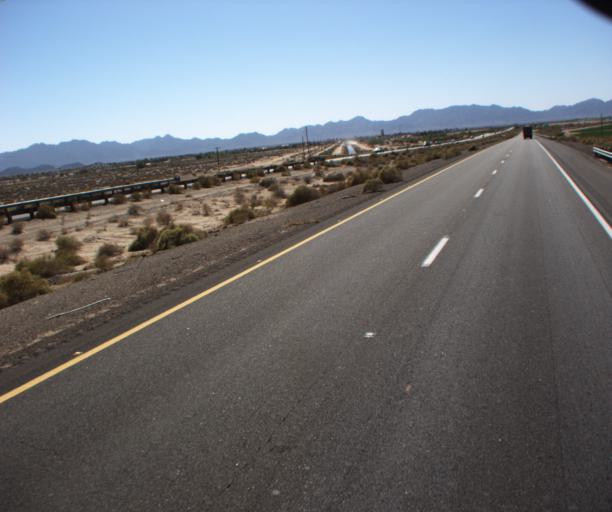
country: US
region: Arizona
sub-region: Yuma County
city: Wellton
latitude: 32.6647
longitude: -114.1308
